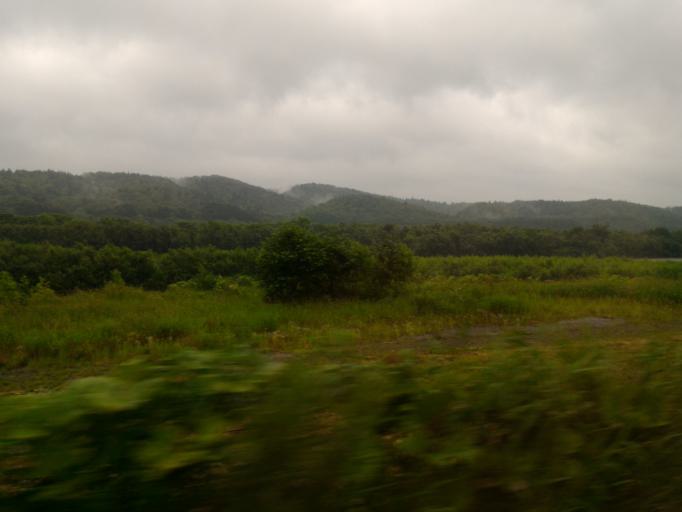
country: JP
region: Hokkaido
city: Nayoro
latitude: 44.7560
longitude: 142.0481
